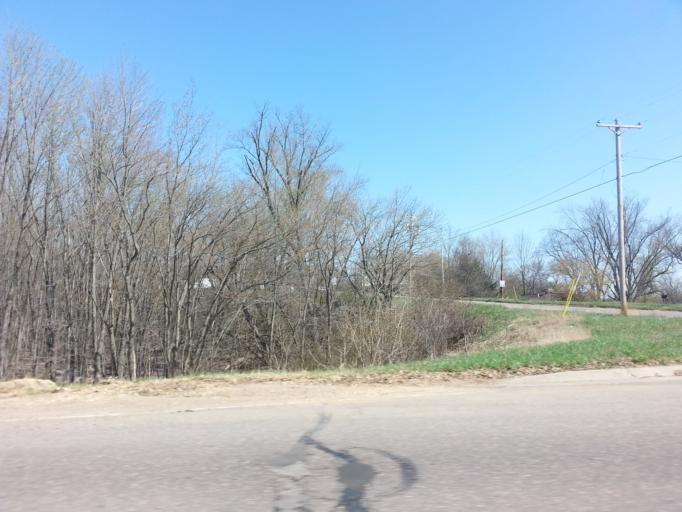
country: US
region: Wisconsin
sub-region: Dunn County
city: Menomonie
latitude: 44.7751
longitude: -91.9352
